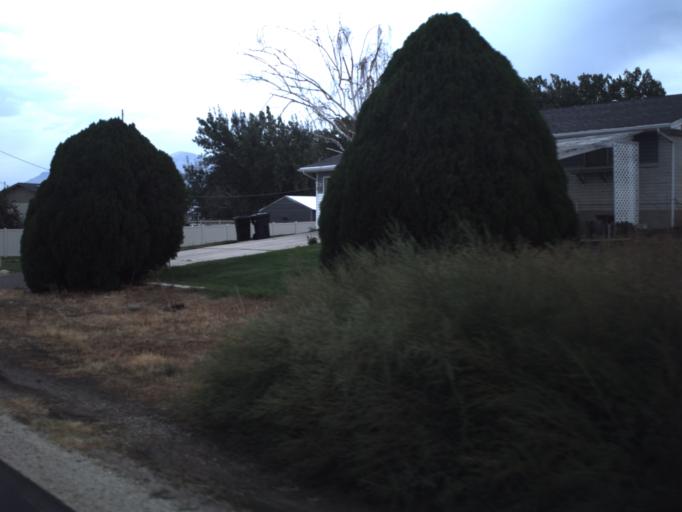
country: US
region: Utah
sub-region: Weber County
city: West Haven
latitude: 41.2131
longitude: -112.0929
